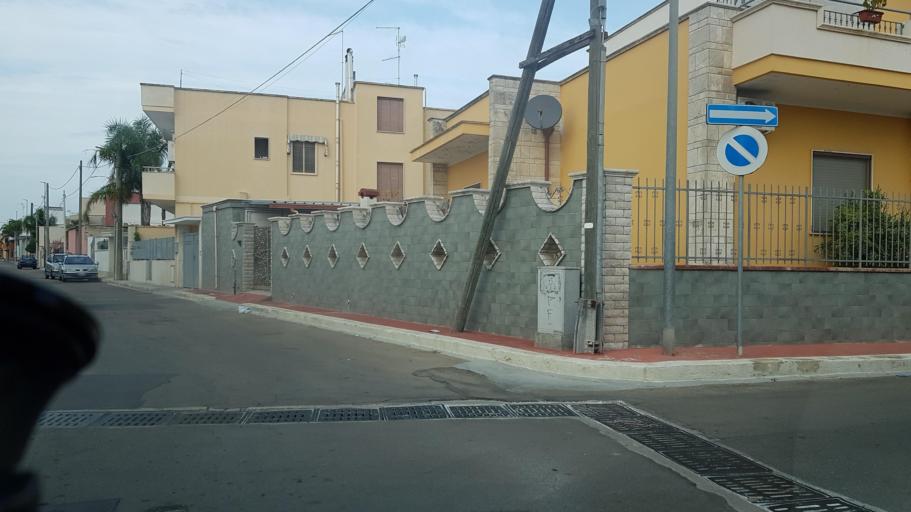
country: IT
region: Apulia
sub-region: Provincia di Lecce
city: Trepuzzi
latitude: 40.4054
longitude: 18.0654
